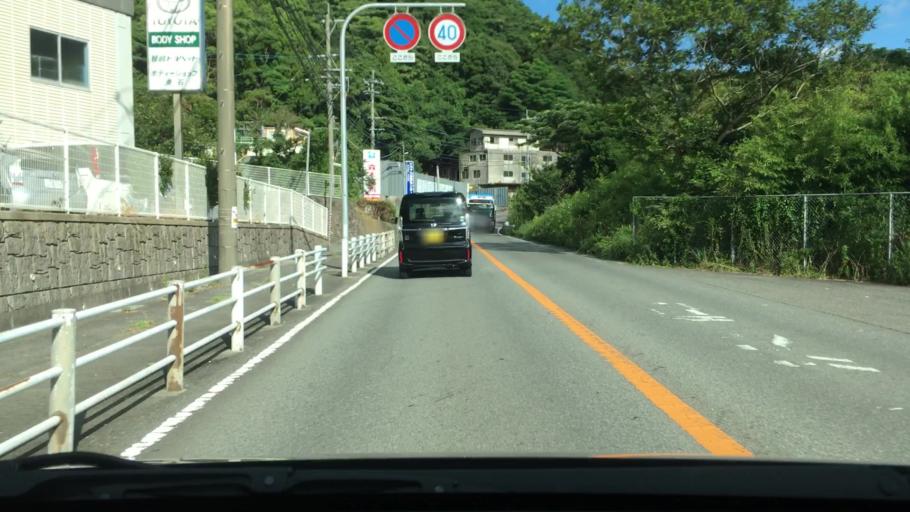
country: JP
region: Nagasaki
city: Togitsu
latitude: 32.8095
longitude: 129.8112
